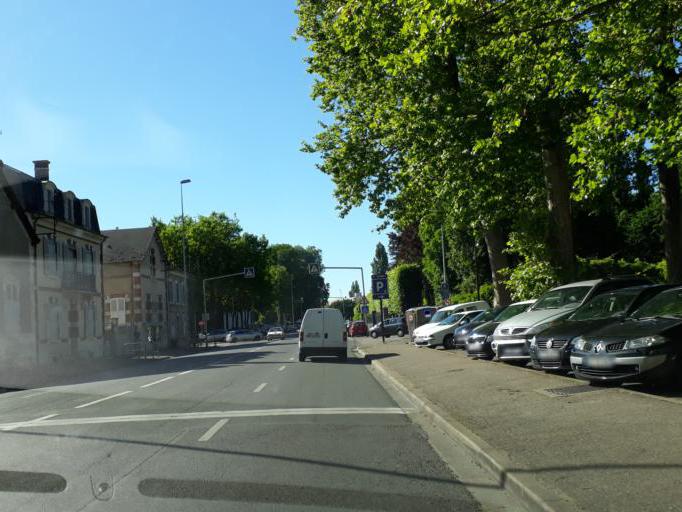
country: FR
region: Centre
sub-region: Departement du Cher
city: Bourges
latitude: 47.0884
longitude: 2.3967
